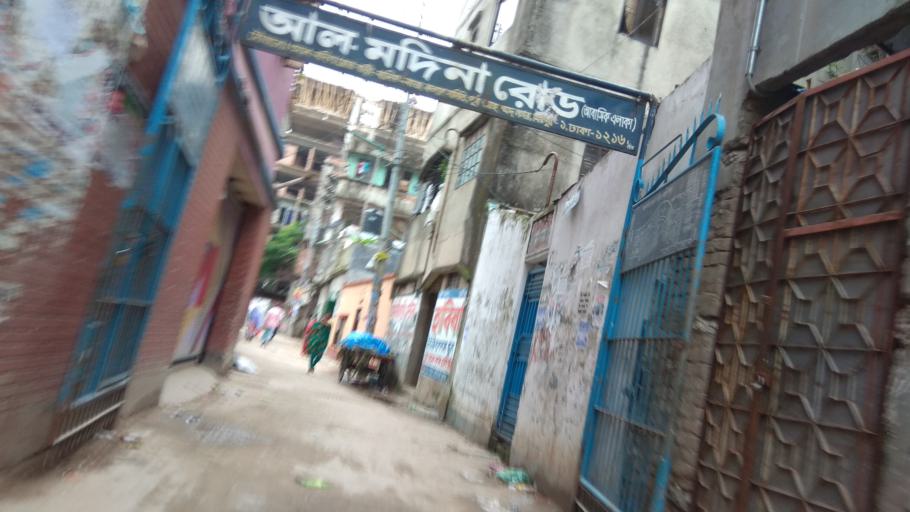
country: BD
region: Dhaka
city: Azimpur
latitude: 23.7985
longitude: 90.3619
